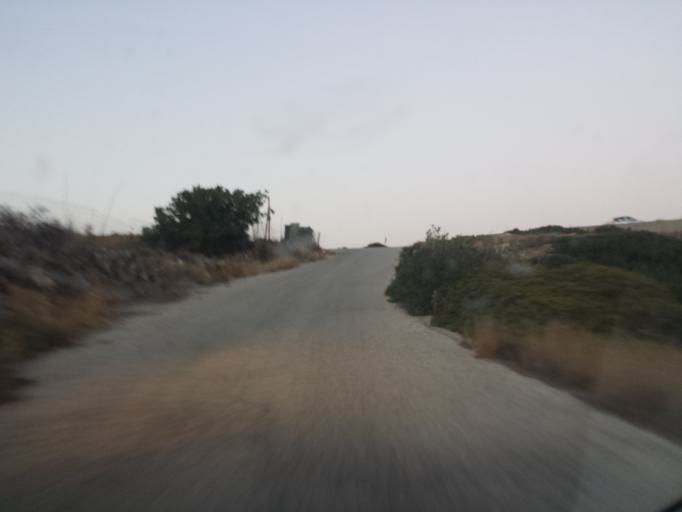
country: GR
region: South Aegean
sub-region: Nomos Kykladon
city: Milos
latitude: 36.7523
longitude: 24.4223
